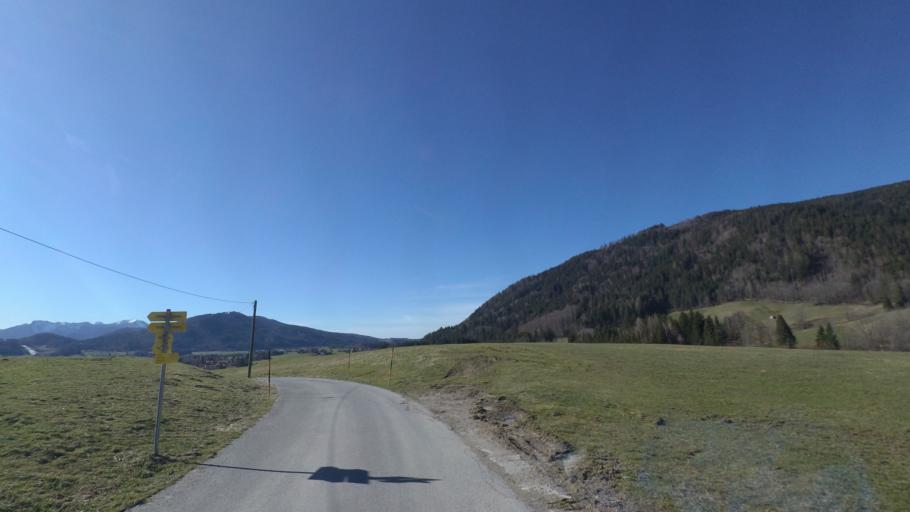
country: DE
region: Bavaria
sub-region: Upper Bavaria
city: Inzell
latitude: 47.7684
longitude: 12.7804
